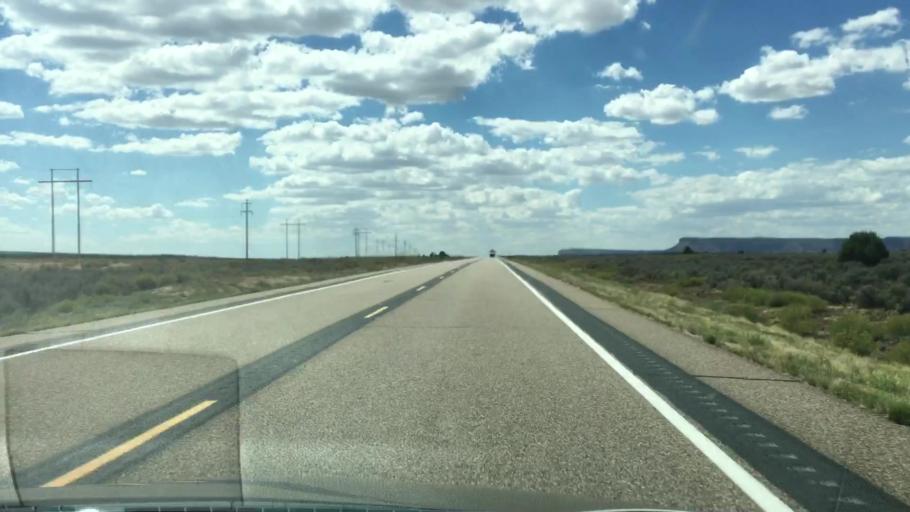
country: US
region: Utah
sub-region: Kane County
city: Kanab
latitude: 37.1629
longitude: -112.0405
